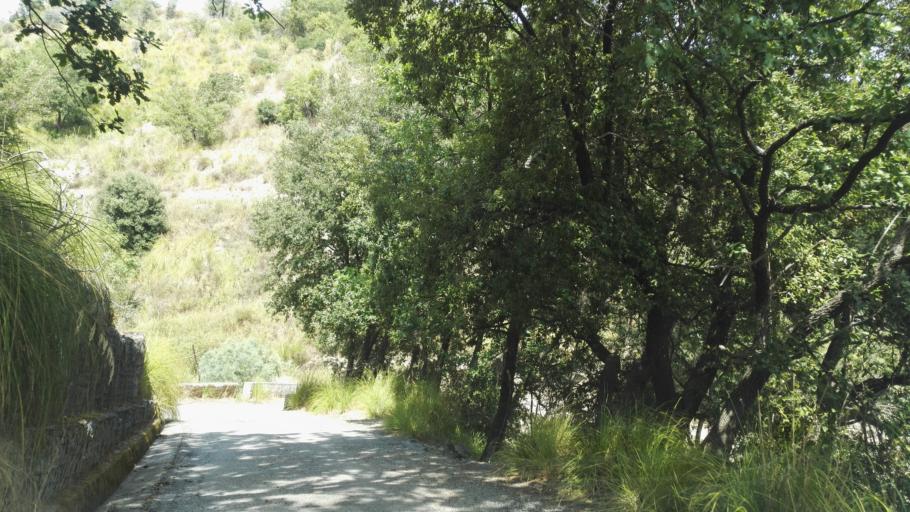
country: IT
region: Calabria
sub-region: Provincia di Reggio Calabria
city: Stilo
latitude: 38.4559
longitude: 16.4622
